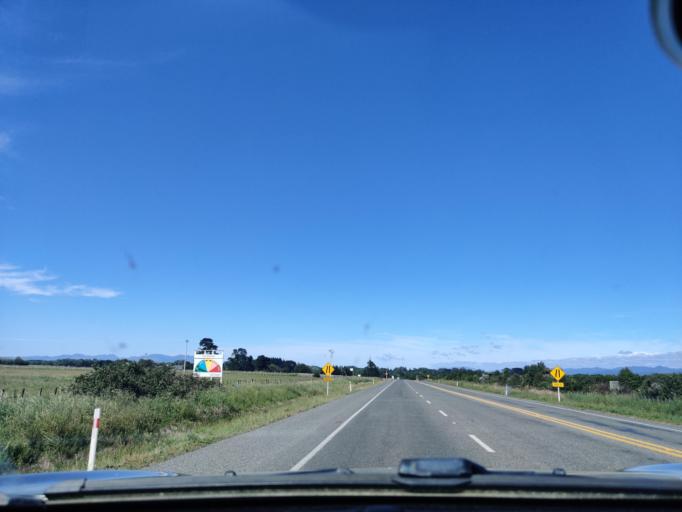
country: NZ
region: Wellington
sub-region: Masterton District
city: Masterton
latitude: -41.0466
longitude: 175.5045
